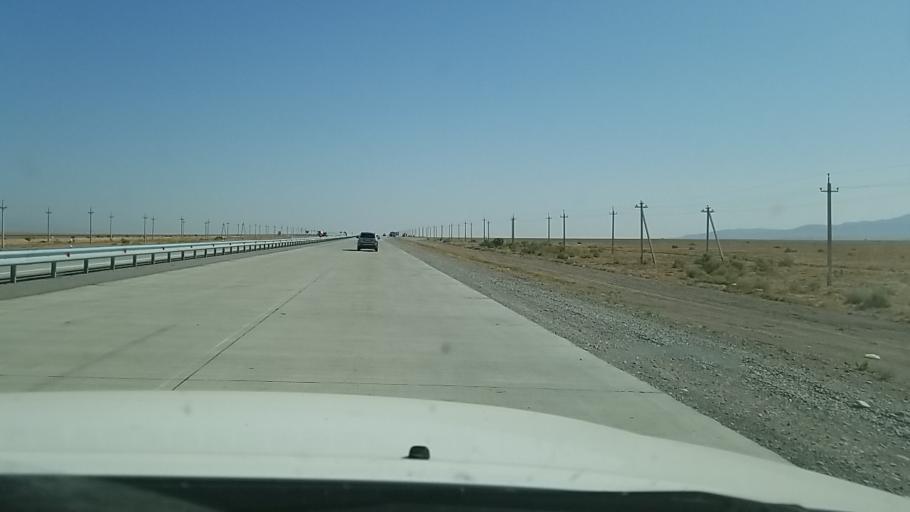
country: KZ
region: Almaty Oblysy
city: Kegen
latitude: 43.7136
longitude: 78.7178
